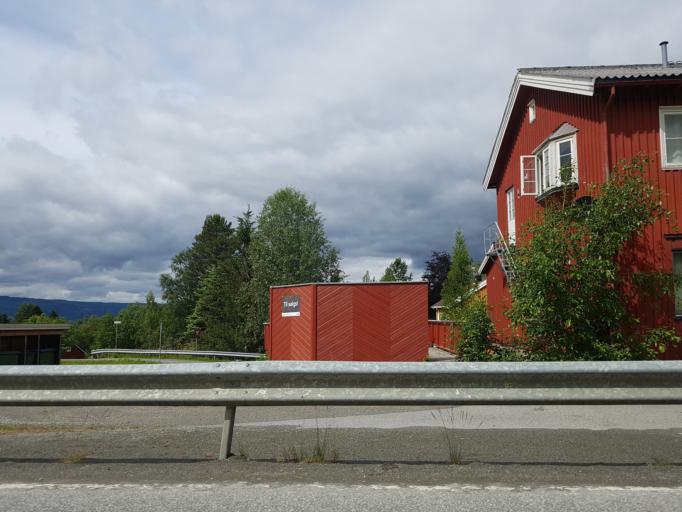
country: NO
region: Sor-Trondelag
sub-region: Selbu
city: Mebonden
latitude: 63.2328
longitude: 11.0378
